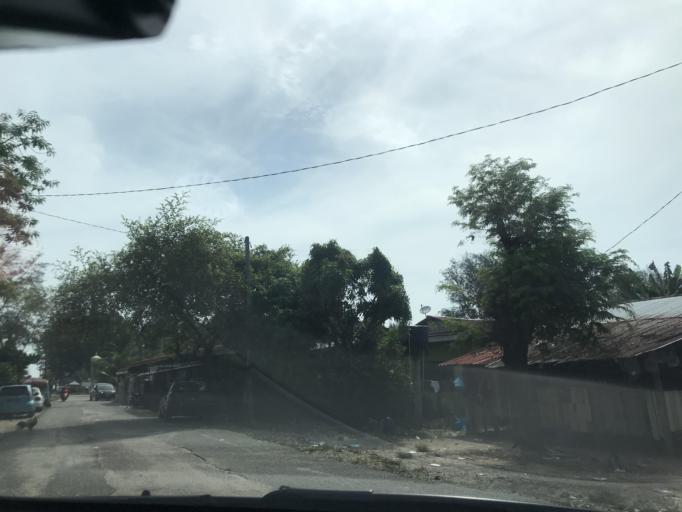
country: MY
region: Kelantan
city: Tumpat
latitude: 6.2230
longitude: 102.1171
